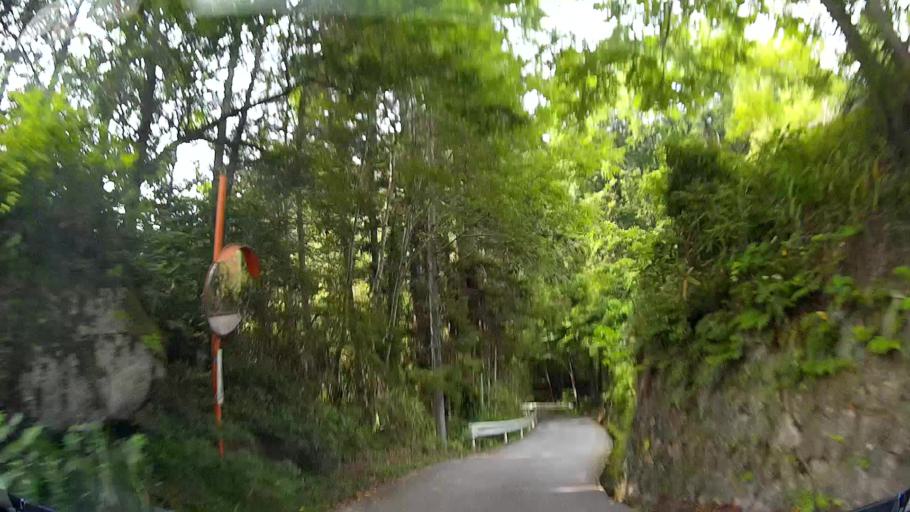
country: JP
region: Nagano
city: Iida
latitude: 35.4948
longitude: 137.8940
